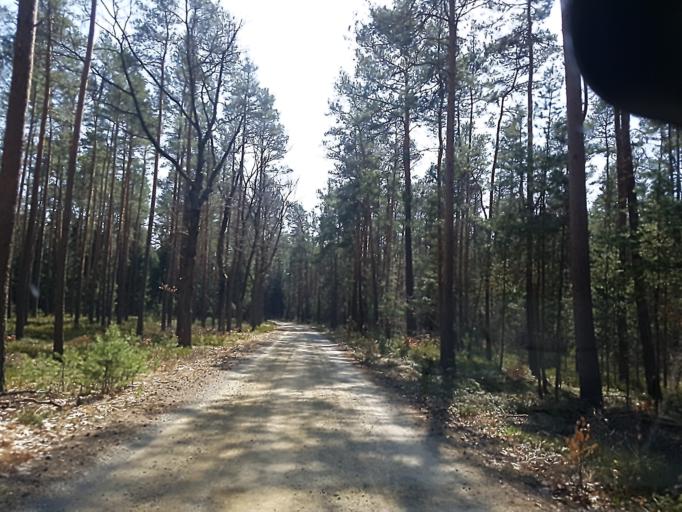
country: DE
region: Brandenburg
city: Schonborn
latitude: 51.5728
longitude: 13.4828
